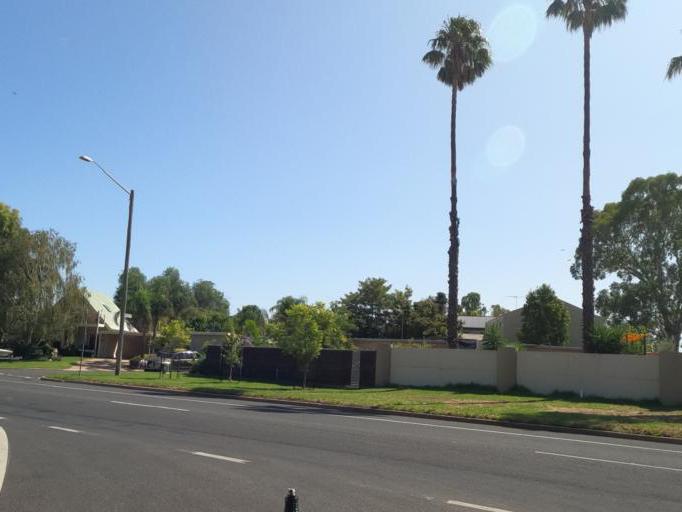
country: AU
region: New South Wales
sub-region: Corowa Shire
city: Mulwala
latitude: -36.0008
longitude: 146.0012
